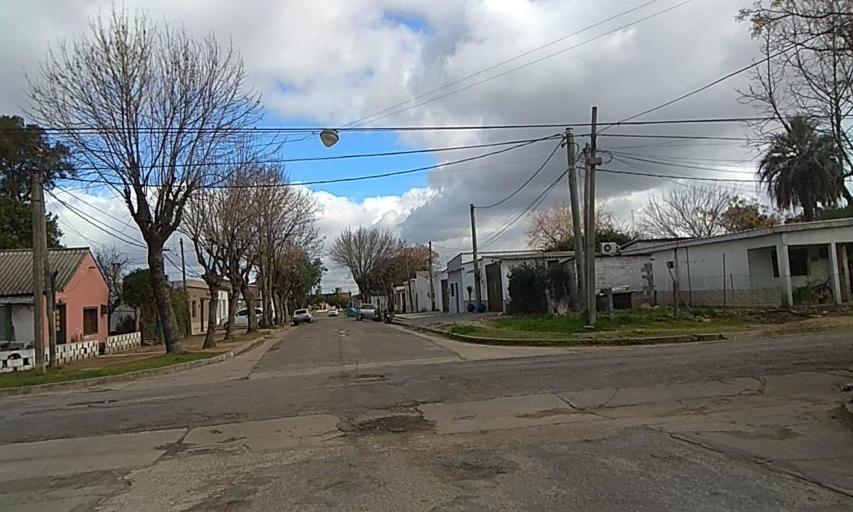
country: UY
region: Florida
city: Florida
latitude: -34.1059
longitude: -56.2121
